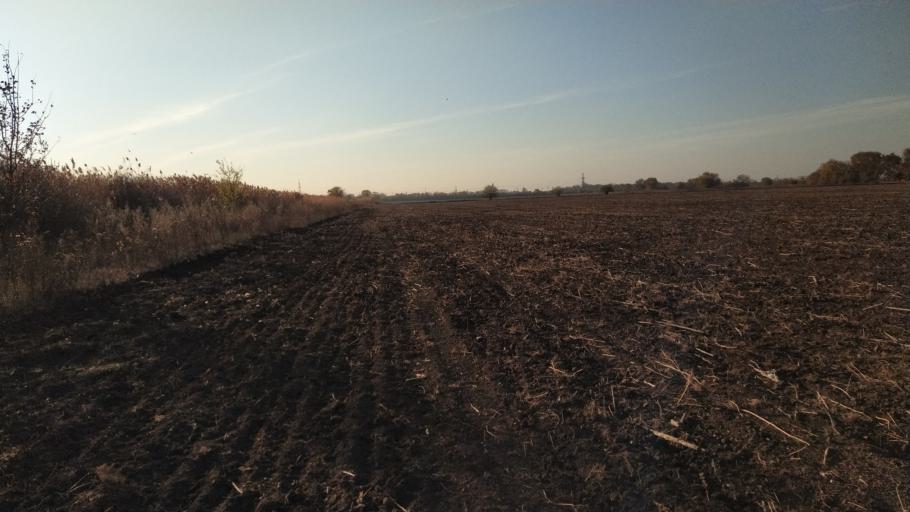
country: RU
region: Rostov
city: Bataysk
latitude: 47.1215
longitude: 39.7263
